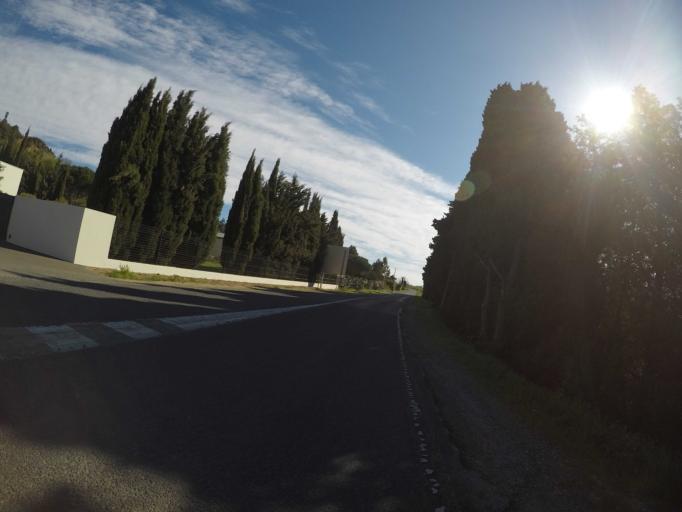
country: FR
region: Languedoc-Roussillon
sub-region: Departement des Pyrenees-Orientales
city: Millas
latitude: 42.6996
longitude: 2.6982
